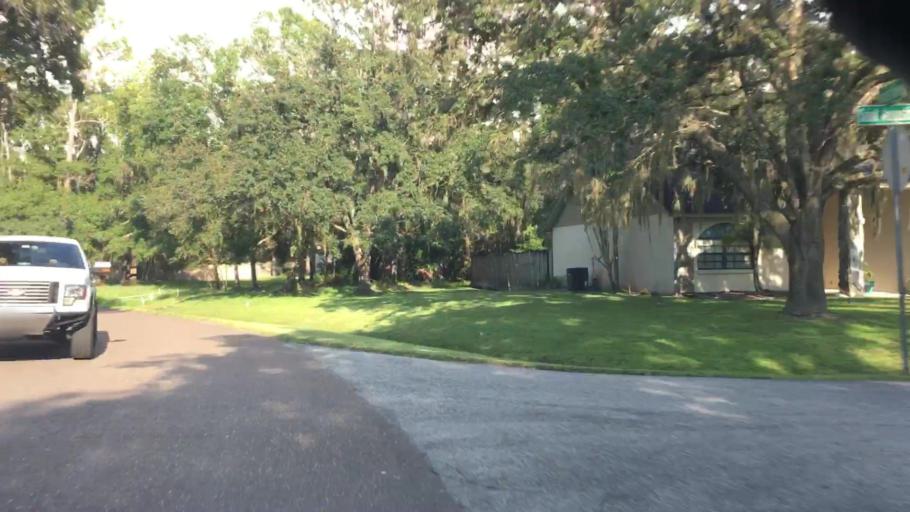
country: US
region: Florida
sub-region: Pasco County
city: Land O' Lakes
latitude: 28.2135
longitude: -82.4238
